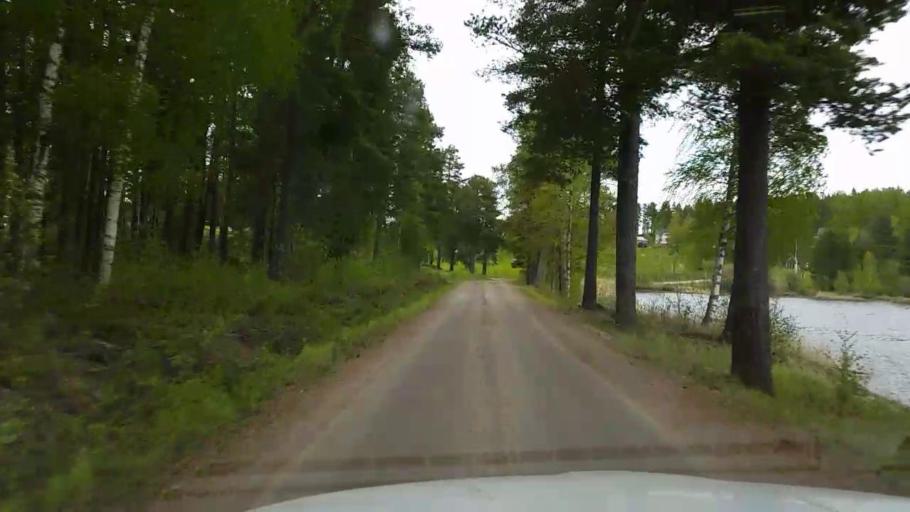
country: SE
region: Vaesternorrland
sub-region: Ange Kommun
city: Ange
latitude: 62.1524
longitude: 15.6739
